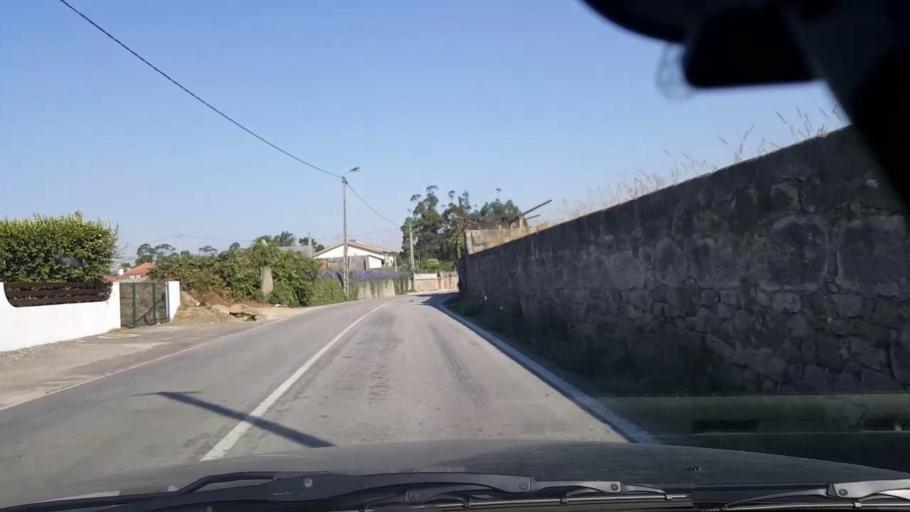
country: PT
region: Porto
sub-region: Maia
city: Gemunde
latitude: 41.2952
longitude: -8.6803
